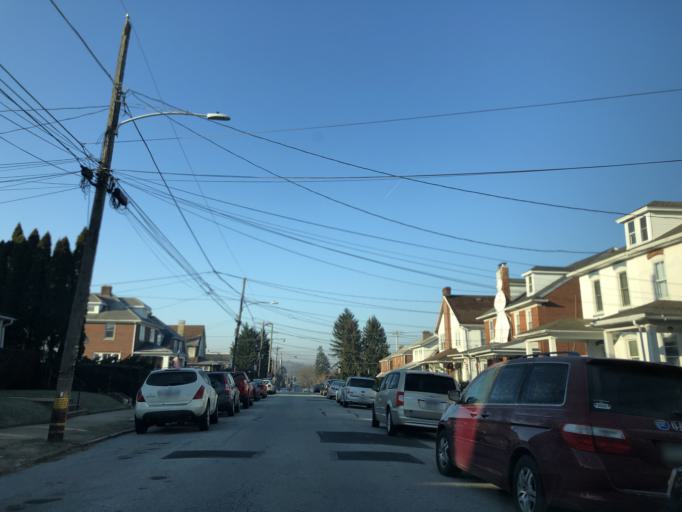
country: US
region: Pennsylvania
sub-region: Chester County
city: Downingtown
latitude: 40.0026
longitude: -75.7132
